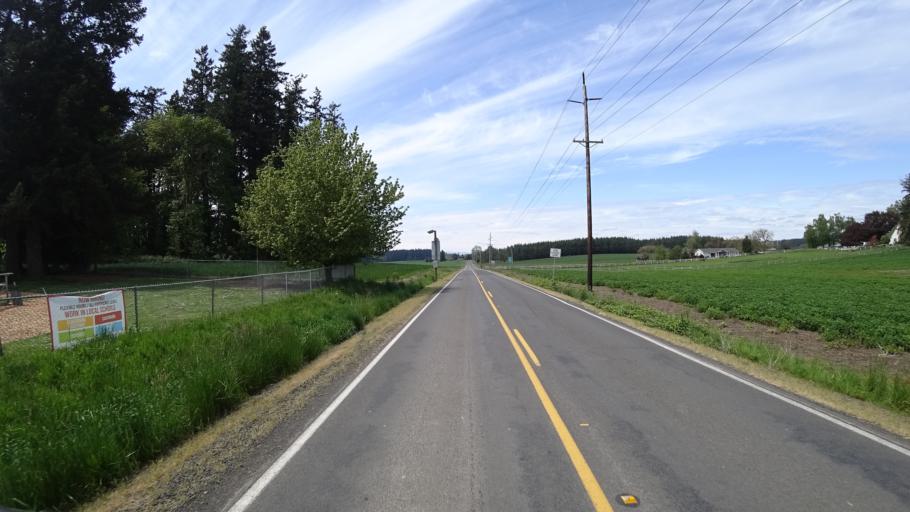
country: US
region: Oregon
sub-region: Washington County
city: Rockcreek
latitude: 45.5780
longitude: -122.9258
